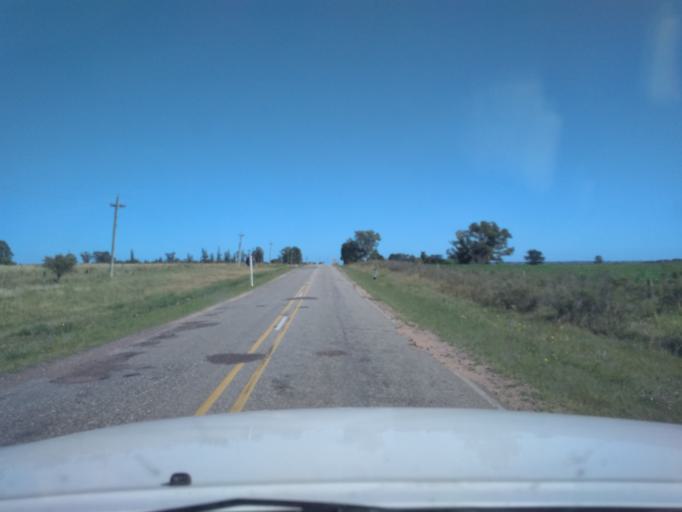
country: UY
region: Canelones
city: San Ramon
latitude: -34.1968
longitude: -55.9361
